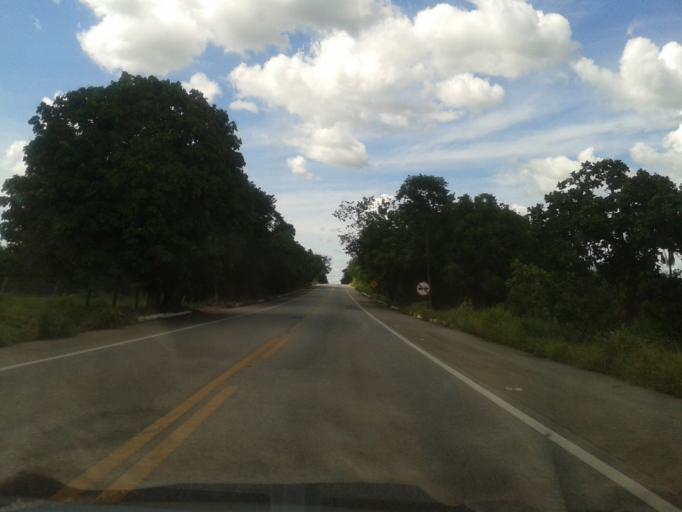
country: BR
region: Goias
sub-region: Itapuranga
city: Itapuranga
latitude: -15.5411
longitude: -50.2897
